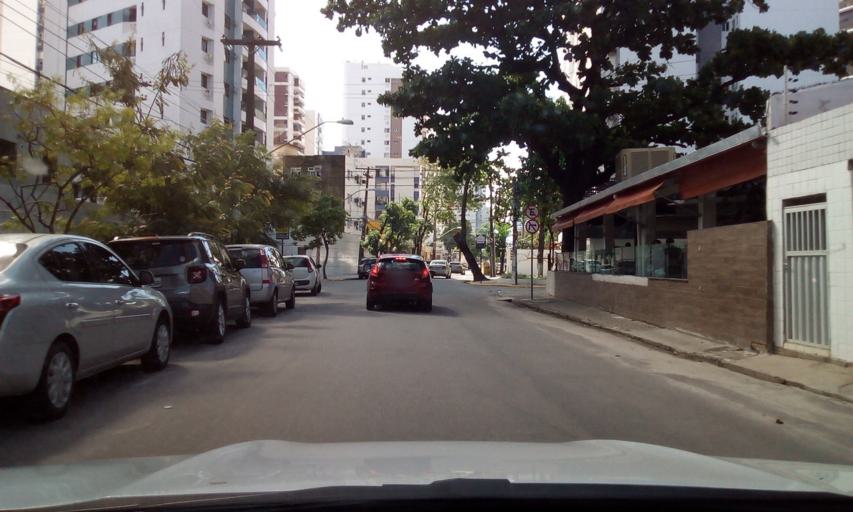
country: BR
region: Pernambuco
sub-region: Recife
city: Recife
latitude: -8.1271
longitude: -34.9036
